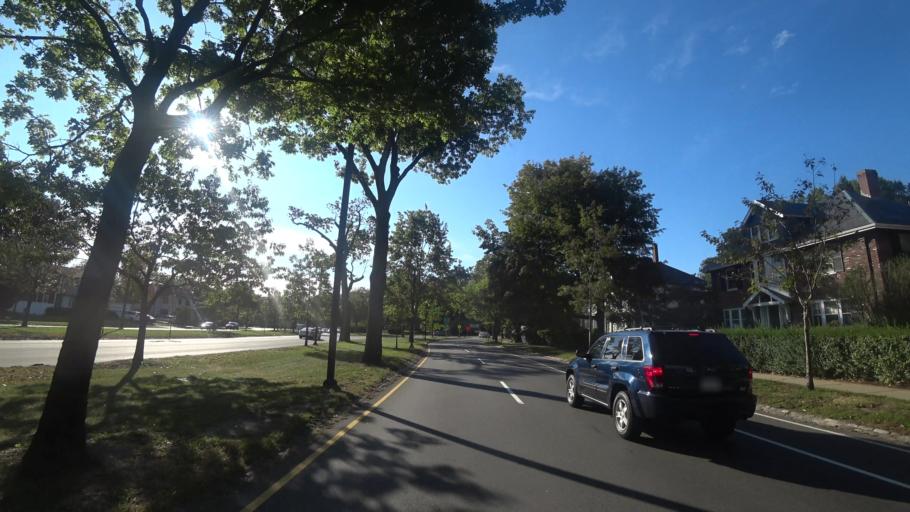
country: US
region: Massachusetts
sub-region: Suffolk County
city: Jamaica Plain
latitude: 42.3105
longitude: -71.1225
